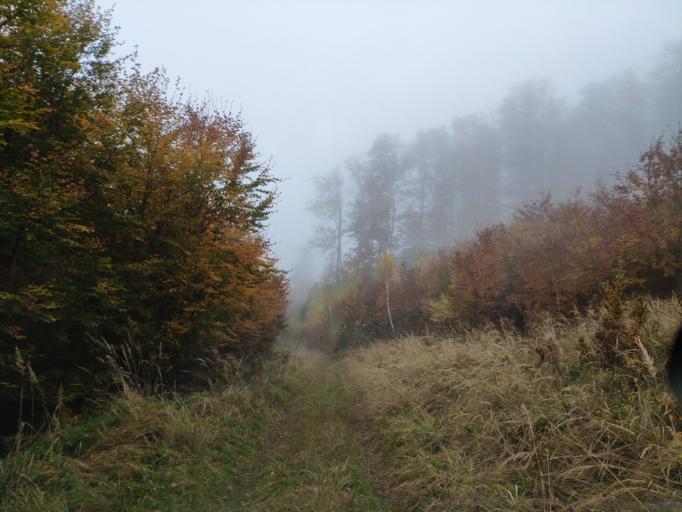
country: SK
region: Kosicky
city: Medzev
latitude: 48.7354
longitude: 20.9942
